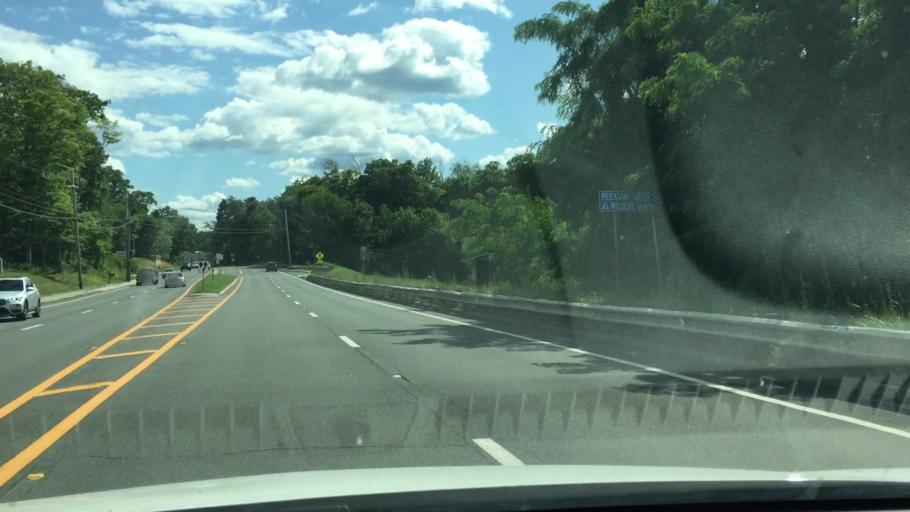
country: US
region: Massachusetts
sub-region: Berkshire County
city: Lenox
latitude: 42.3837
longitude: -73.2753
